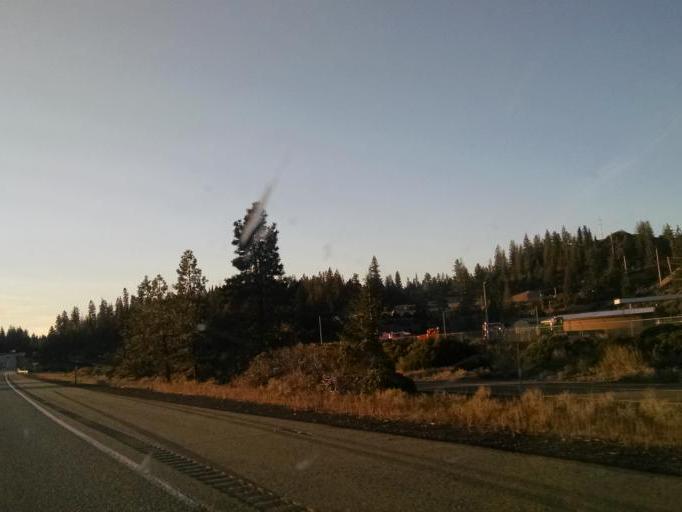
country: US
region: California
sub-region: Siskiyou County
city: Weed
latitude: 41.3670
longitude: -122.3689
